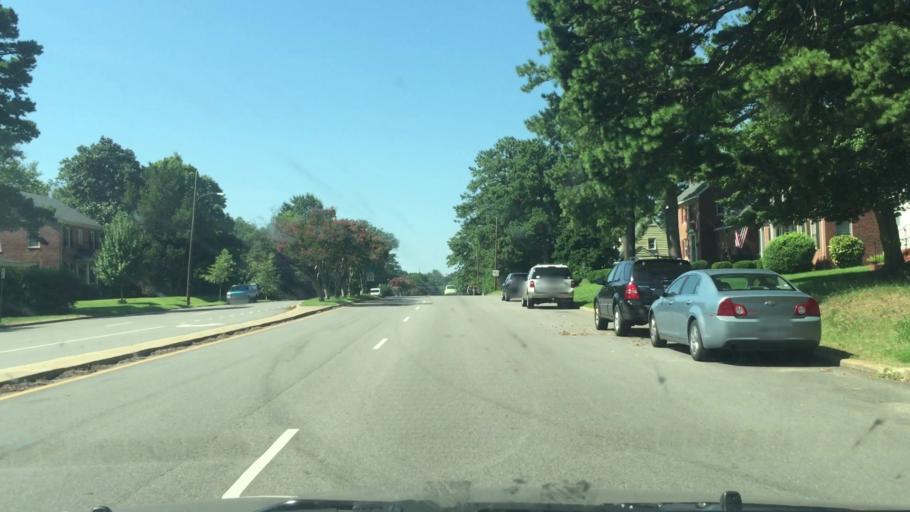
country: US
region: Virginia
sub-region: Henrico County
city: Dumbarton
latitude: 37.5823
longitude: -77.5115
